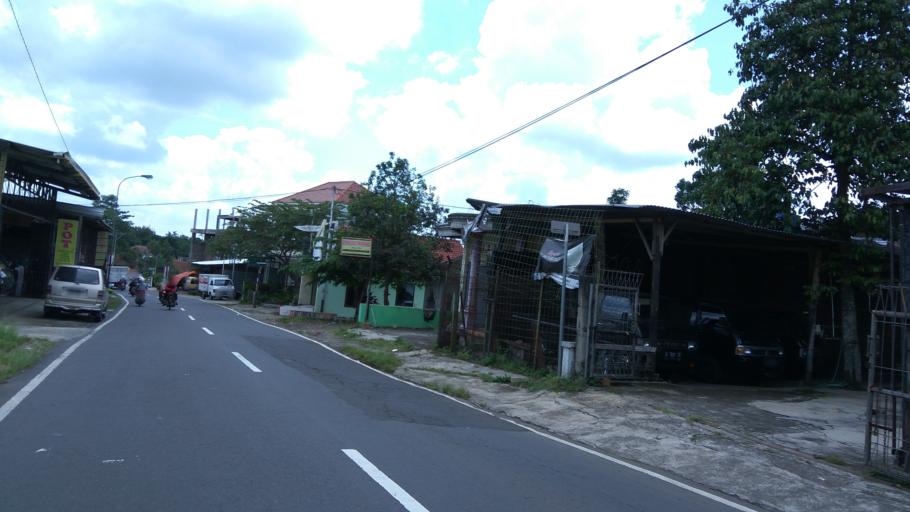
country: ID
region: Central Java
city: Ambarawa
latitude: -7.2381
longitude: 110.3883
